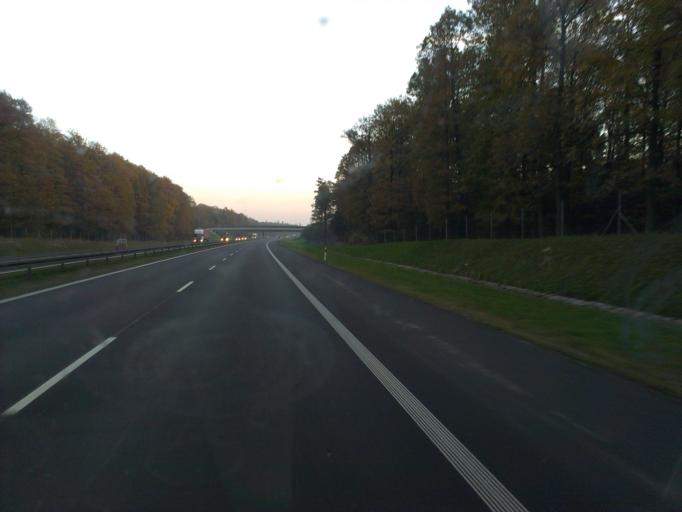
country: PL
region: Opole Voivodeship
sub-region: Powiat opolski
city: Proszkow
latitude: 50.5528
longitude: 17.8878
